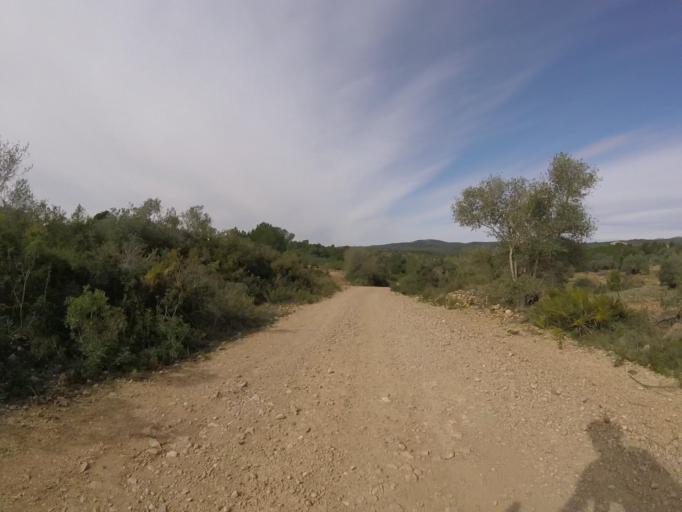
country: ES
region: Valencia
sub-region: Provincia de Castello
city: Torreblanca
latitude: 40.2042
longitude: 0.1454
